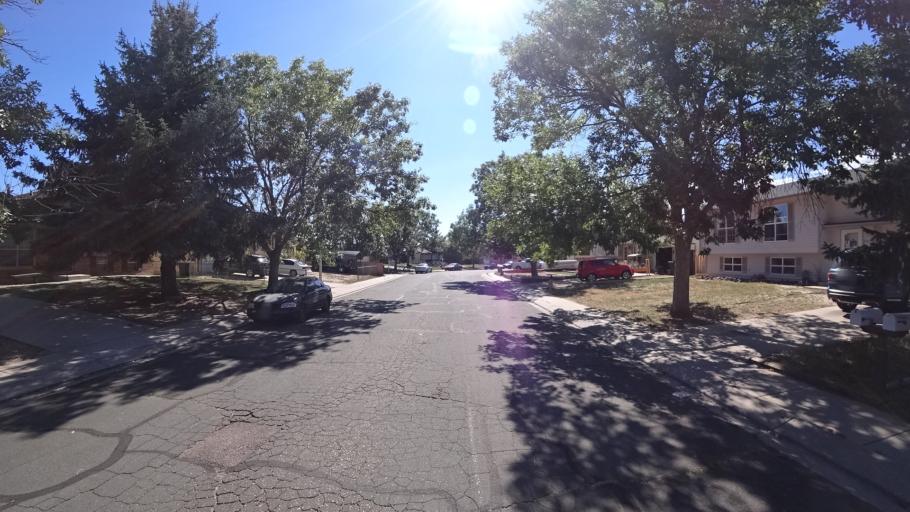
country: US
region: Colorado
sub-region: El Paso County
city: Stratmoor
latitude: 38.7901
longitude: -104.7414
